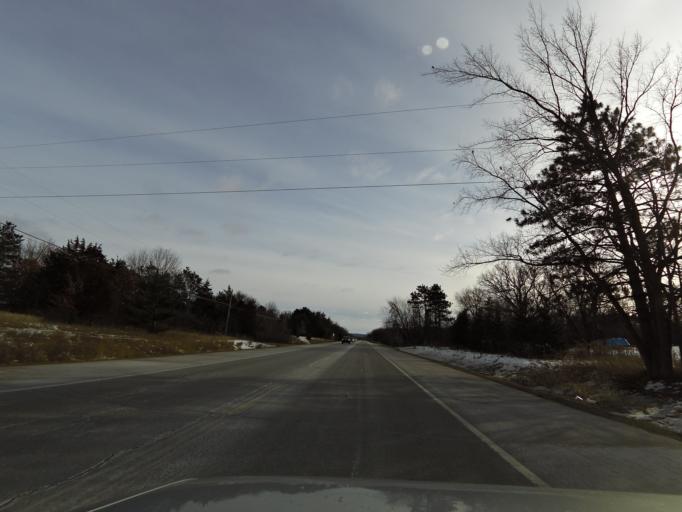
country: US
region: Wisconsin
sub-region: Saint Croix County
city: Hudson
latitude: 44.9765
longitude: -92.7762
